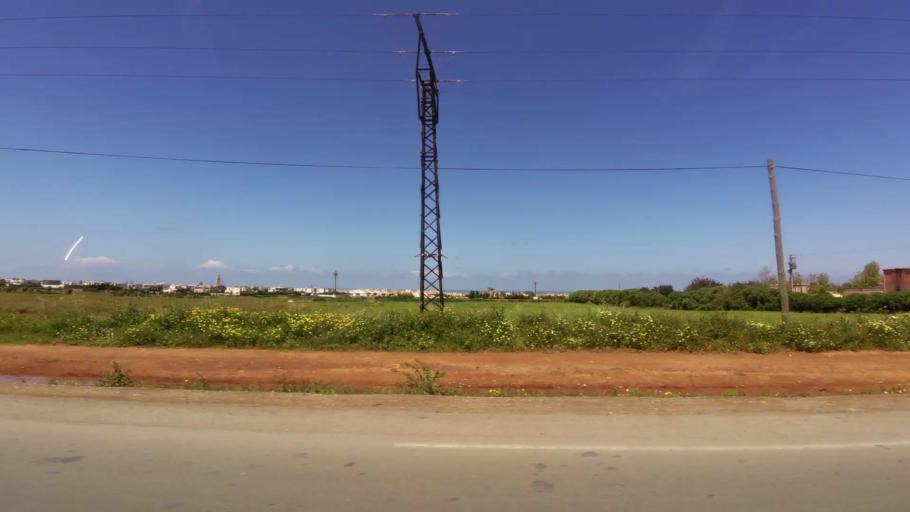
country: MA
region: Grand Casablanca
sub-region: Nouaceur
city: Dar Bouazza
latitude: 33.5303
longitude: -7.7735
